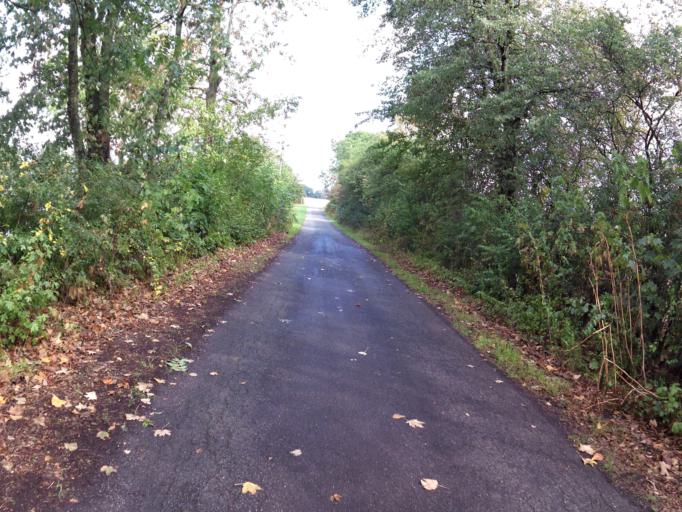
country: DE
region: Lower Saxony
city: Schweringen
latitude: 52.7247
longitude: 9.1954
